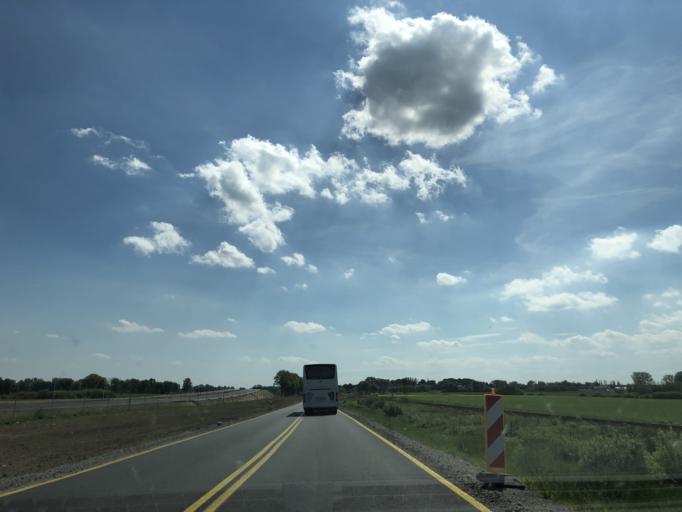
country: PL
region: West Pomeranian Voivodeship
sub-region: Powiat gryficki
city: Ploty
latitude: 53.7300
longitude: 15.2003
